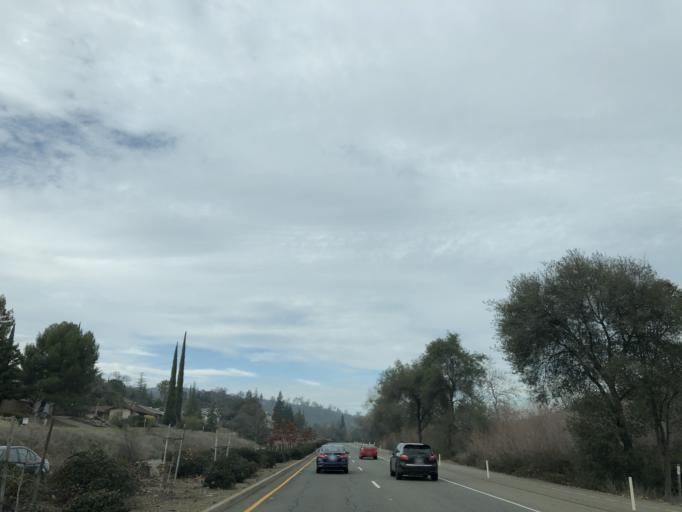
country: US
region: California
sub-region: El Dorado County
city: El Dorado Hills
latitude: 38.6616
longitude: -121.0728
